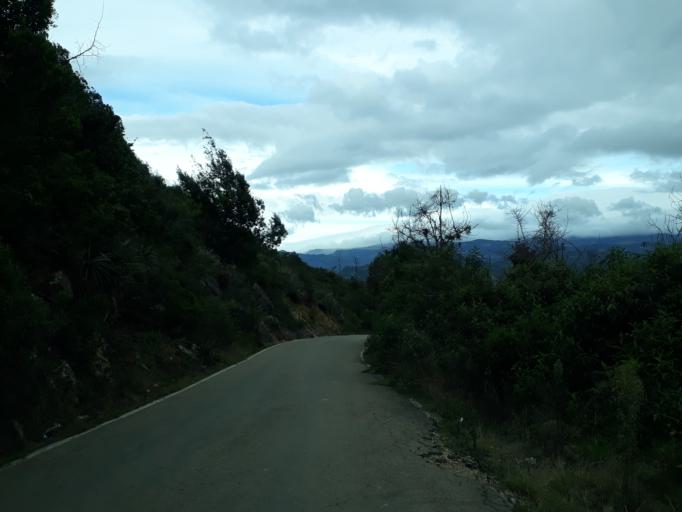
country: CO
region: Cundinamarca
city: Susa
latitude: 5.3961
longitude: -73.7843
